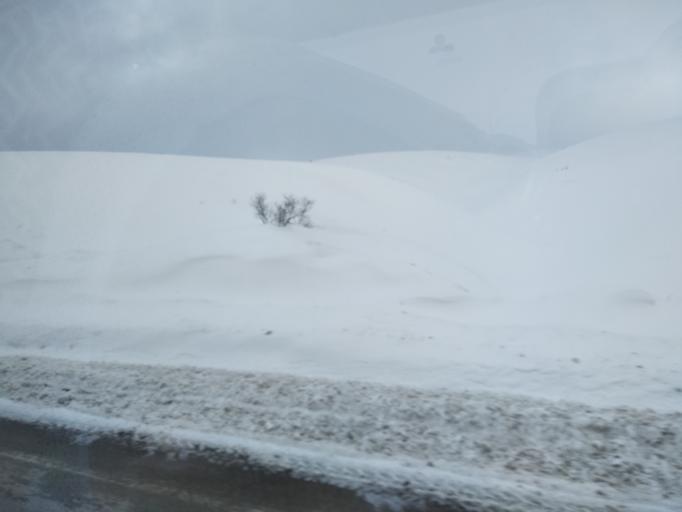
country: TR
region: Erzincan
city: Catalarmut
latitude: 39.8895
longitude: 39.3581
